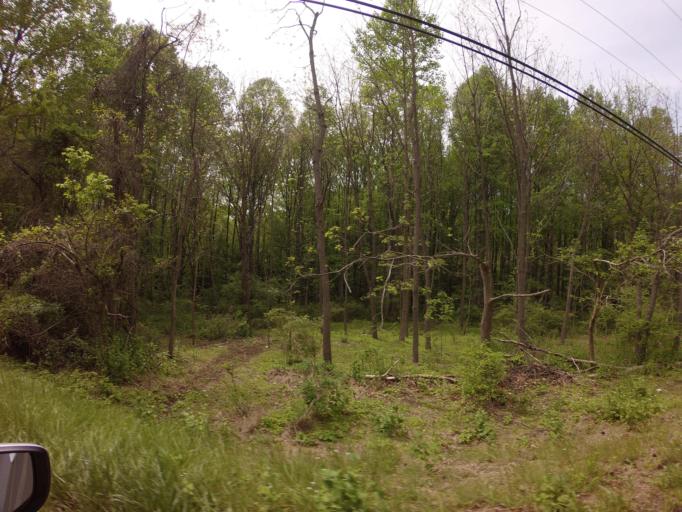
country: US
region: Maryland
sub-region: Carroll County
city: Eldersburg
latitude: 39.4560
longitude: -76.9558
